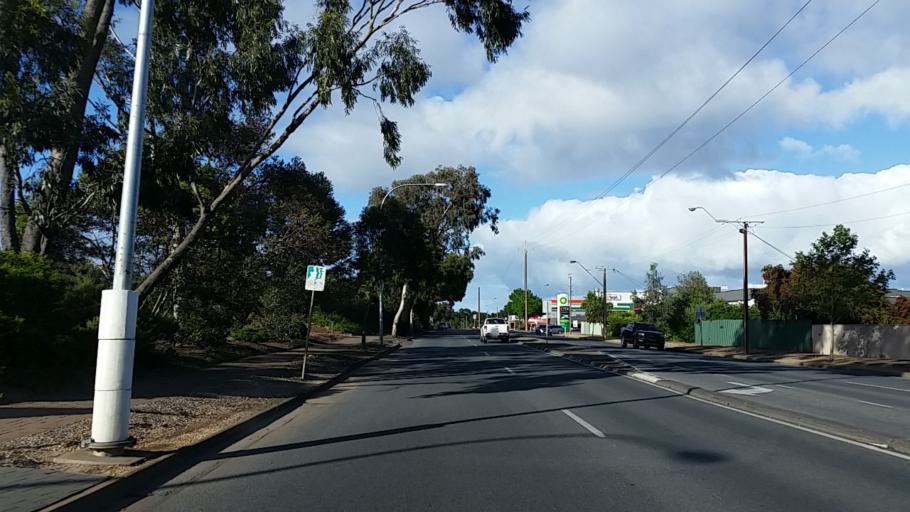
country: AU
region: South Australia
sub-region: Mitcham
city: Clapham
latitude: -35.0001
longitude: 138.5926
